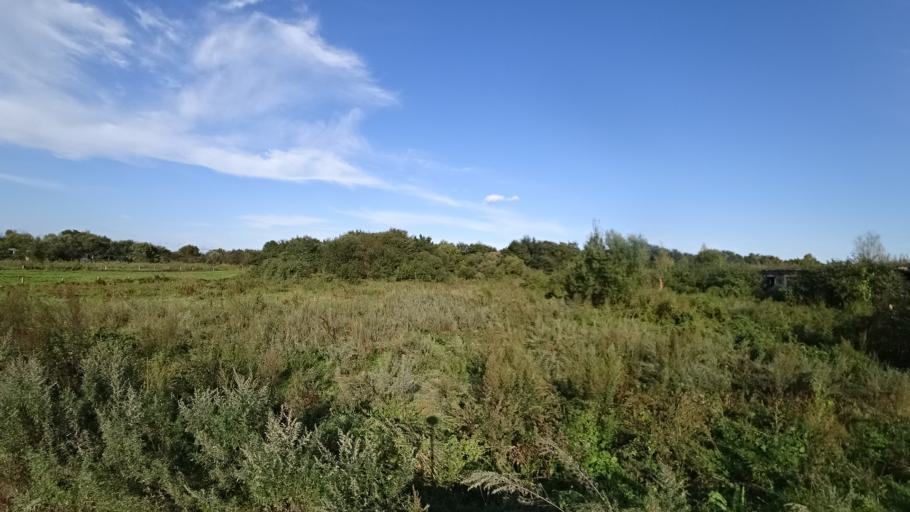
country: RU
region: Amur
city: Arkhara
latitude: 49.3479
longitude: 130.1068
